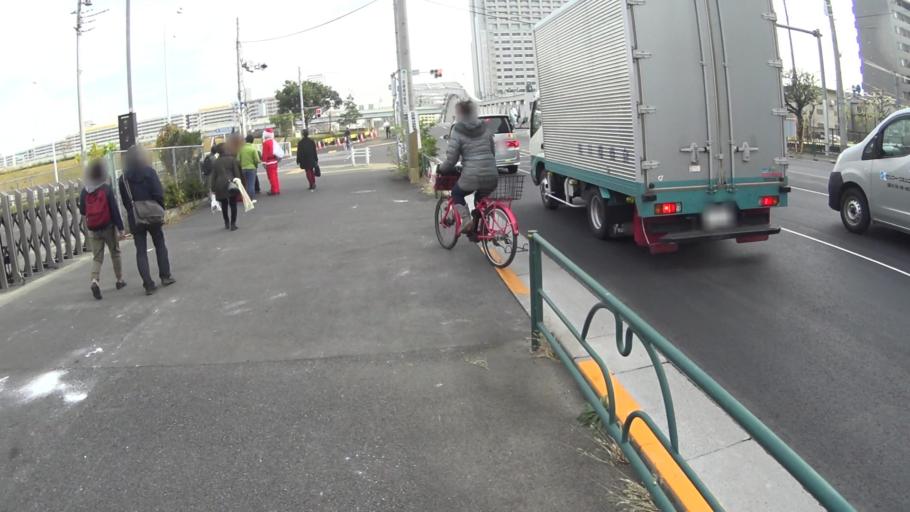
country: JP
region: Saitama
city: Soka
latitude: 35.7284
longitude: 139.8078
